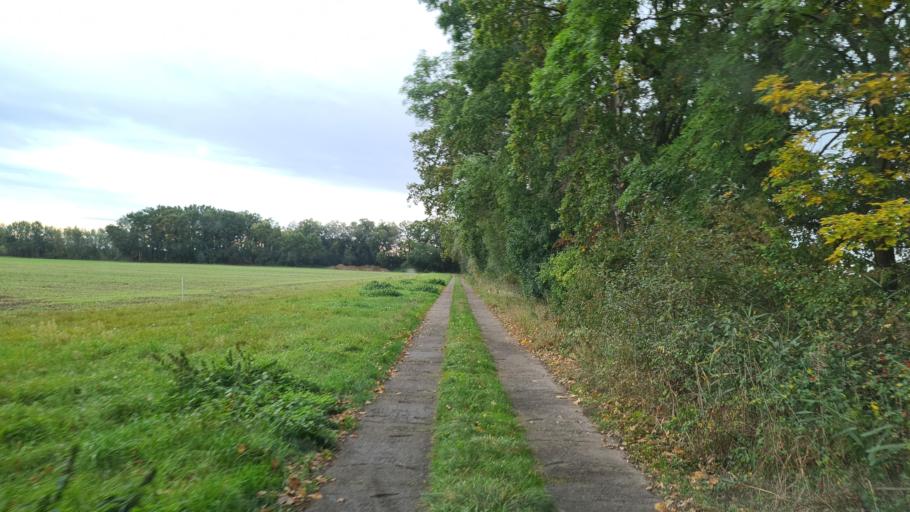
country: DE
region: Brandenburg
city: Zossen
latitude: 52.2499
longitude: 13.4669
